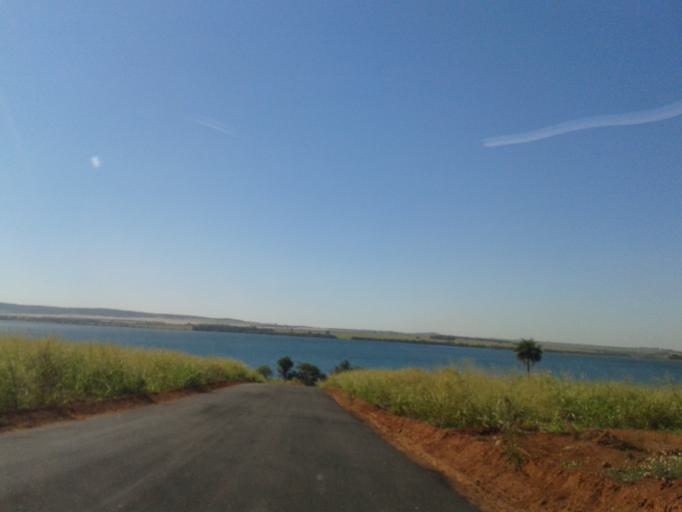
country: BR
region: Minas Gerais
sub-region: Capinopolis
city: Capinopolis
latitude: -18.5346
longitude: -49.4984
